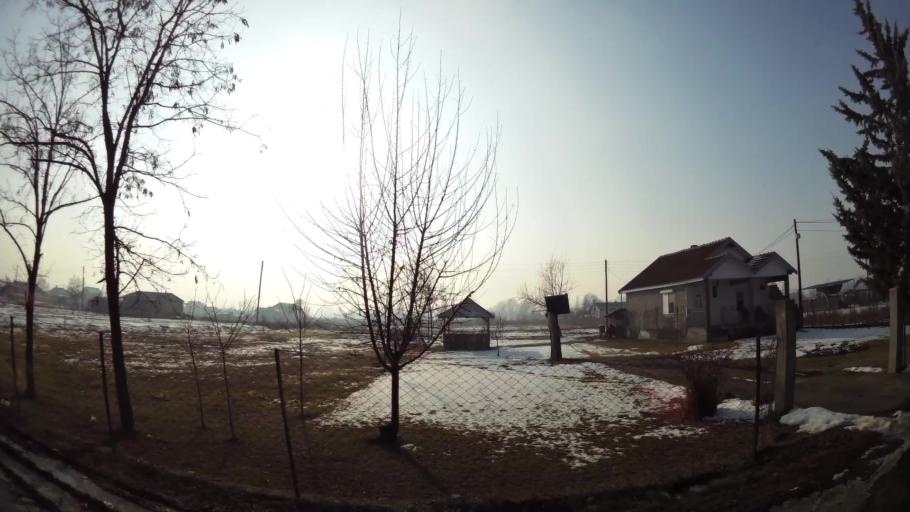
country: MK
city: Kadino
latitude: 41.9618
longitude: 21.5999
